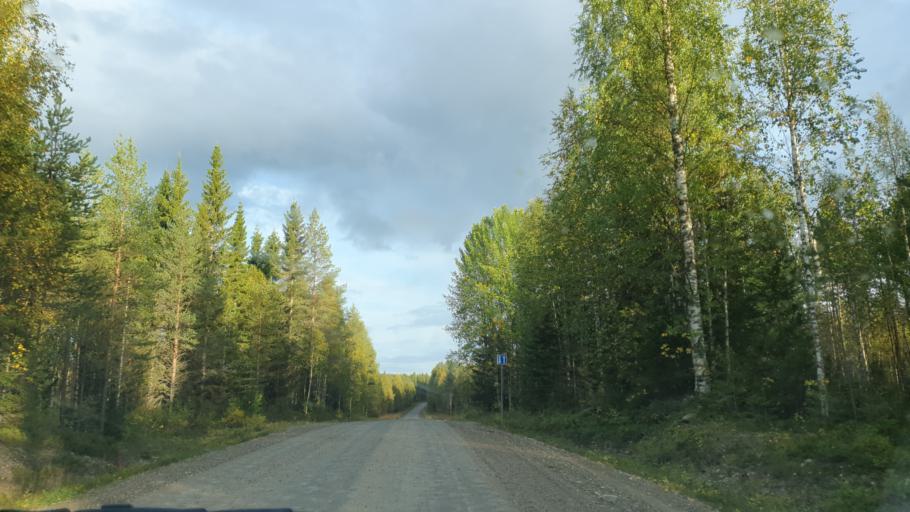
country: FI
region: Kainuu
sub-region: Kehys-Kainuu
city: Kuhmo
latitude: 64.4199
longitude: 29.3686
